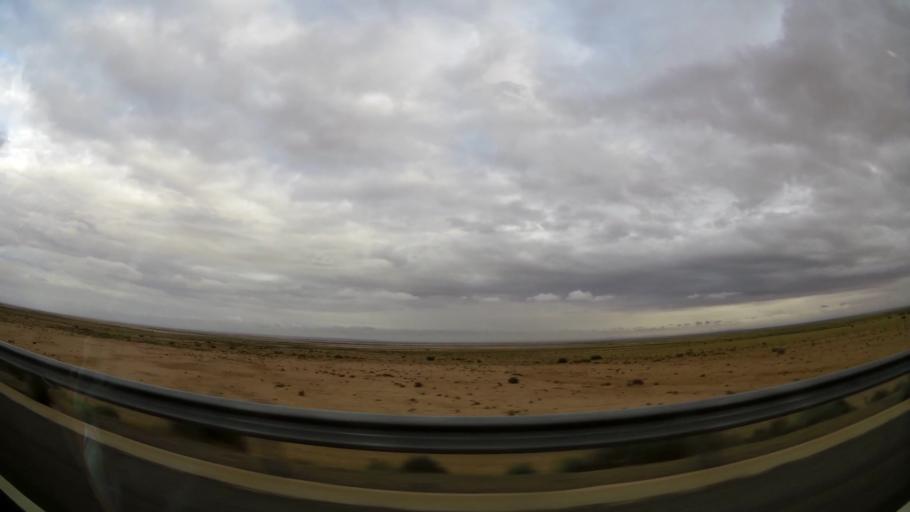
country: MA
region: Taza-Al Hoceima-Taounate
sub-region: Taza
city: Guercif
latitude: 34.3198
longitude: -3.5798
